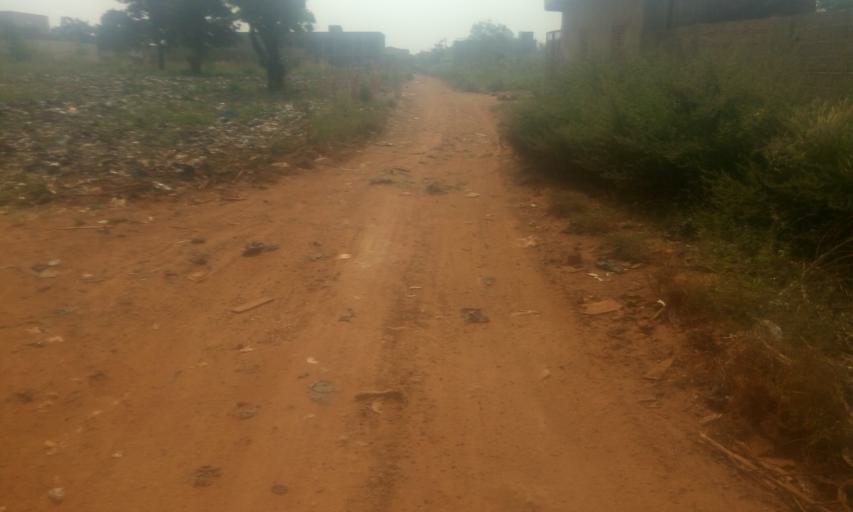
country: ML
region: Bamako
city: Bamako
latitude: 12.5830
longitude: -8.0803
